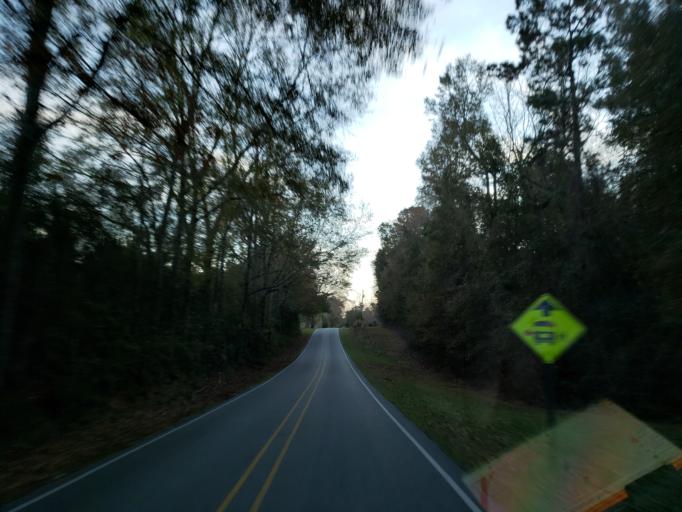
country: US
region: Mississippi
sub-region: Forrest County
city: Hattiesburg
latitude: 31.2461
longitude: -89.3140
